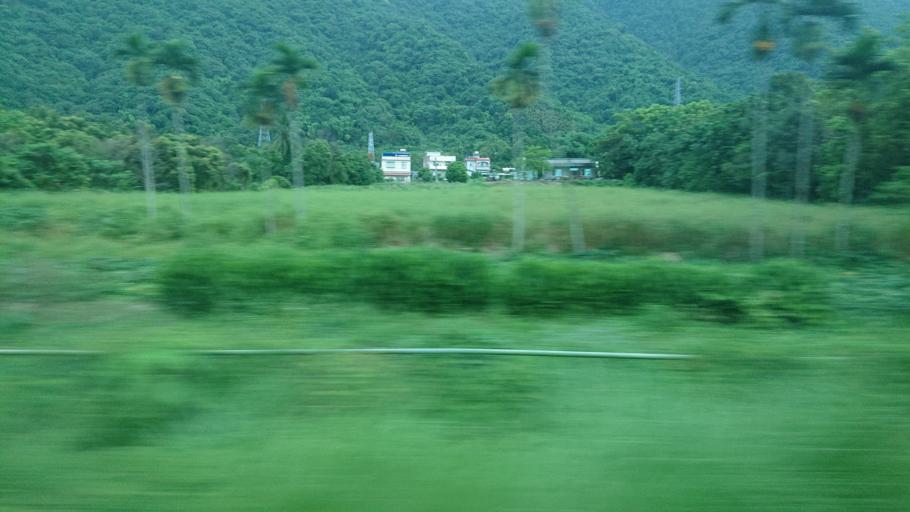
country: TW
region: Taiwan
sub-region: Hualien
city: Hualian
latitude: 24.1118
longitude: 121.6225
